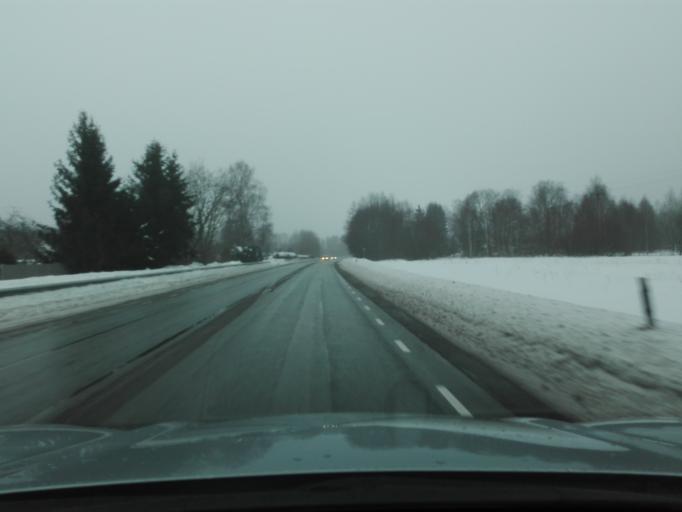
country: EE
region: Harju
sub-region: Kiili vald
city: Kiili
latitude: 59.3302
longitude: 24.7728
